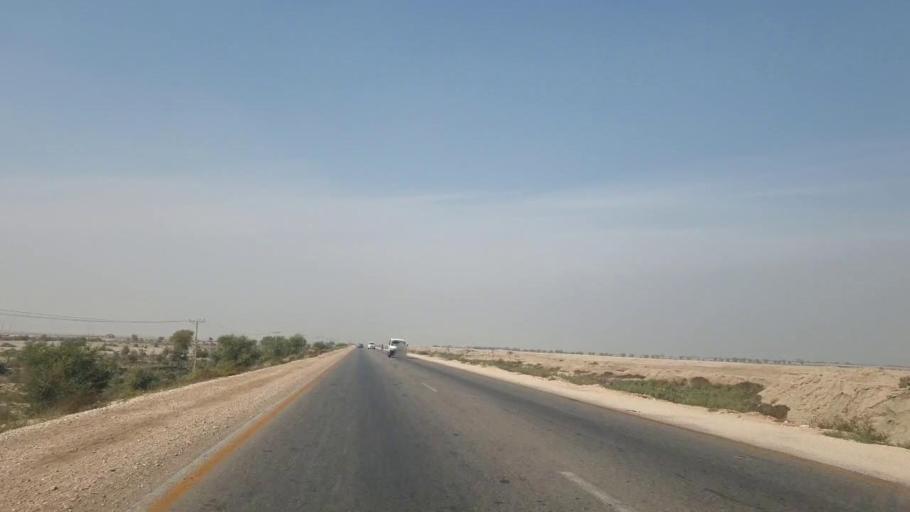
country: PK
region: Sindh
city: Sann
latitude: 25.9074
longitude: 68.2275
